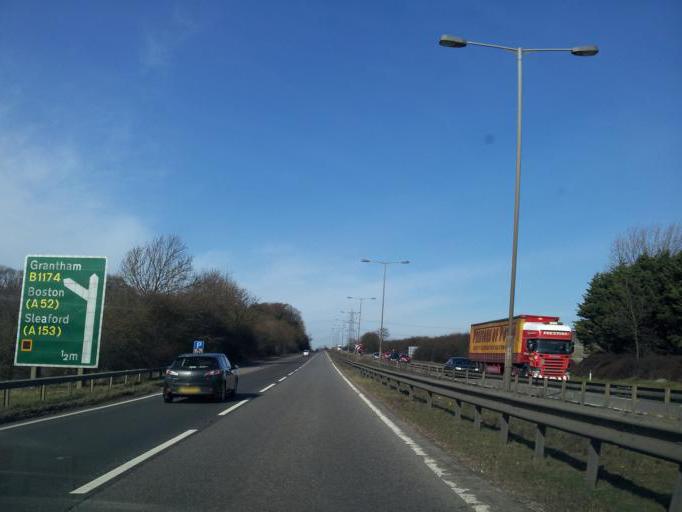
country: GB
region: England
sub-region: Lincolnshire
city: Grantham
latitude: 52.8649
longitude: -0.6297
